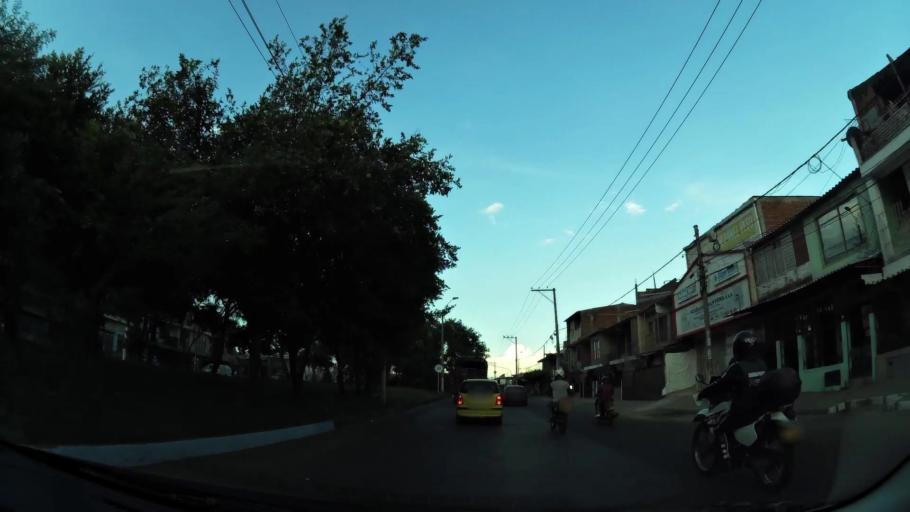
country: CO
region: Valle del Cauca
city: Cali
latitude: 3.4118
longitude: -76.4919
